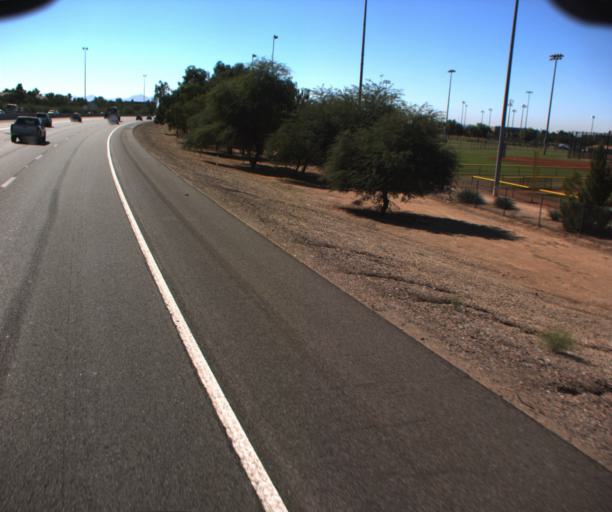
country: US
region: Arizona
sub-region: Maricopa County
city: Peoria
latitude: 33.6184
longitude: -112.2395
